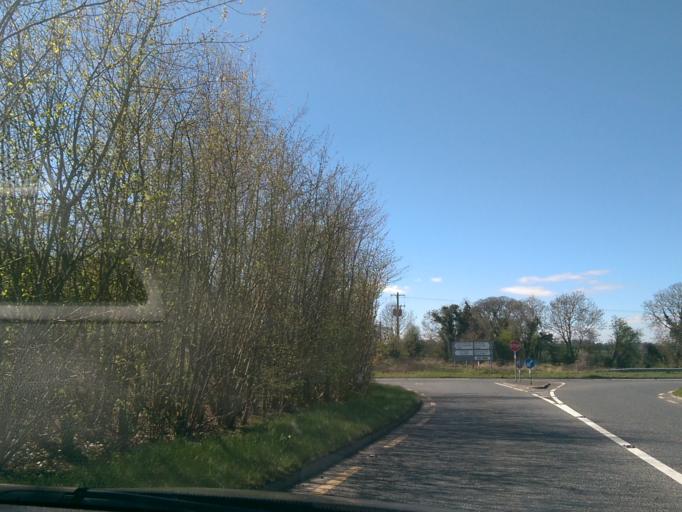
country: IE
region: Leinster
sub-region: Kildare
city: Moone
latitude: 53.0009
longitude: -6.8050
